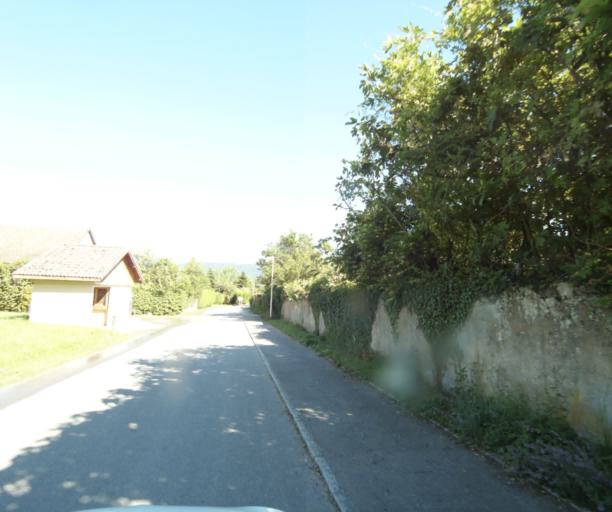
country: FR
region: Rhone-Alpes
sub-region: Departement de la Haute-Savoie
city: Messery
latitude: 46.3327
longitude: 6.3011
